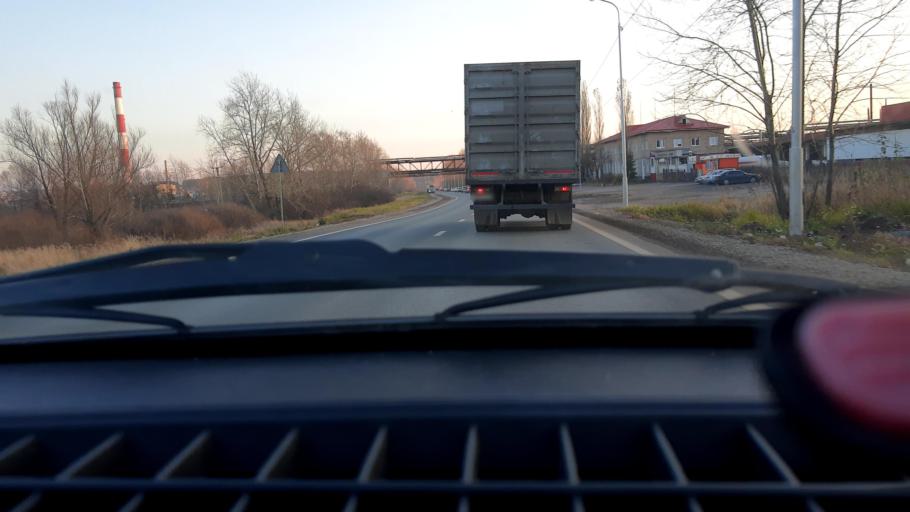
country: RU
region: Bashkortostan
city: Ufa
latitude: 54.8484
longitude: 56.1185
